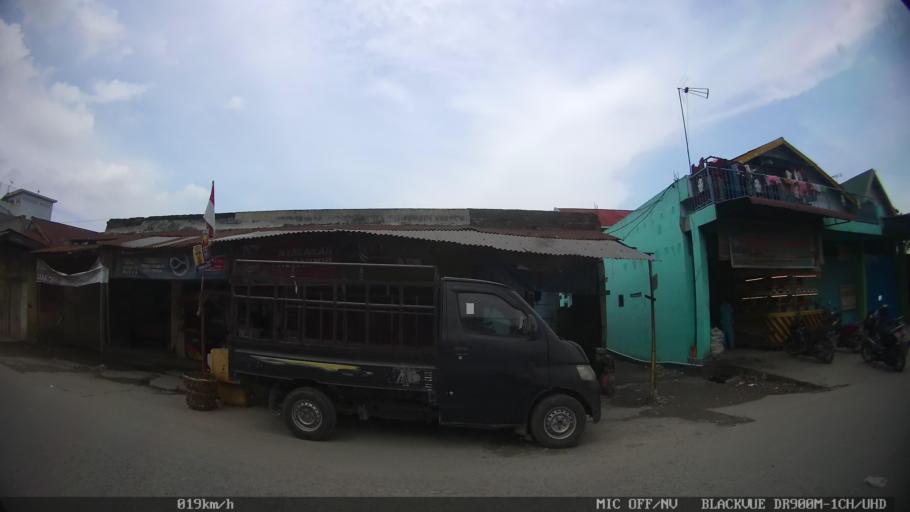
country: ID
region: North Sumatra
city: Labuhan Deli
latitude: 3.6760
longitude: 98.6735
